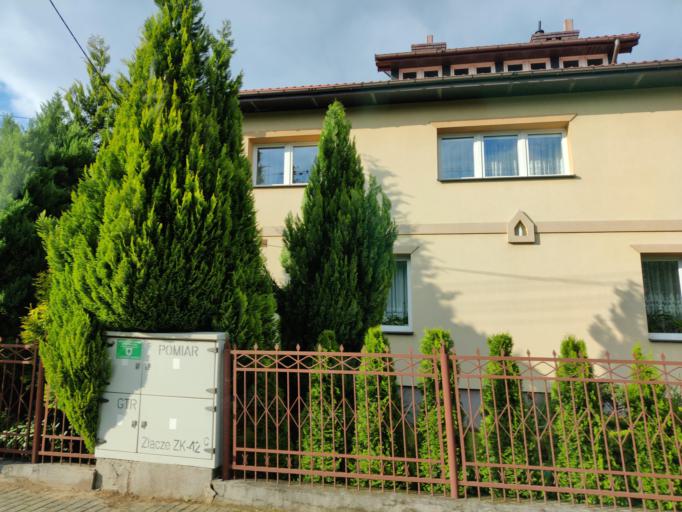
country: PL
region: Masovian Voivodeship
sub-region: Powiat piaseczynski
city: Konstancin-Jeziorna
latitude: 52.1092
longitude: 21.1290
